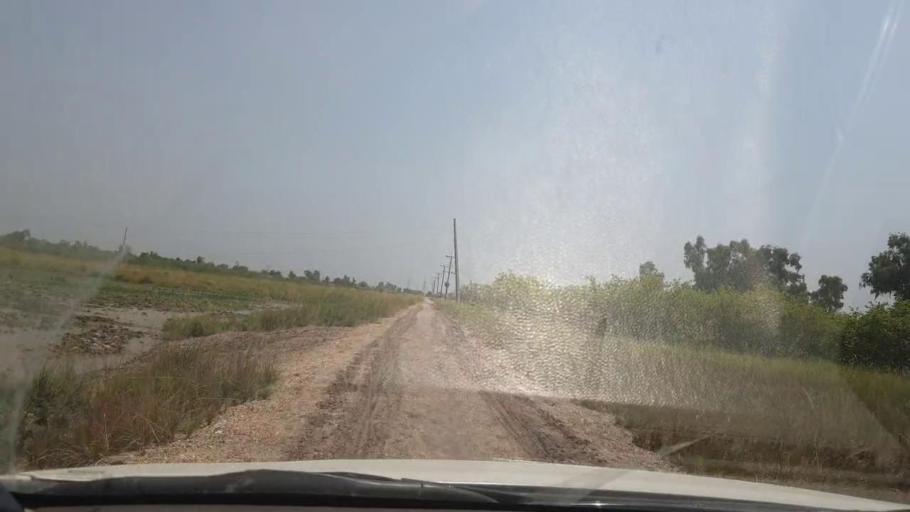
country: PK
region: Sindh
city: Lakhi
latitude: 27.8640
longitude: 68.7009
